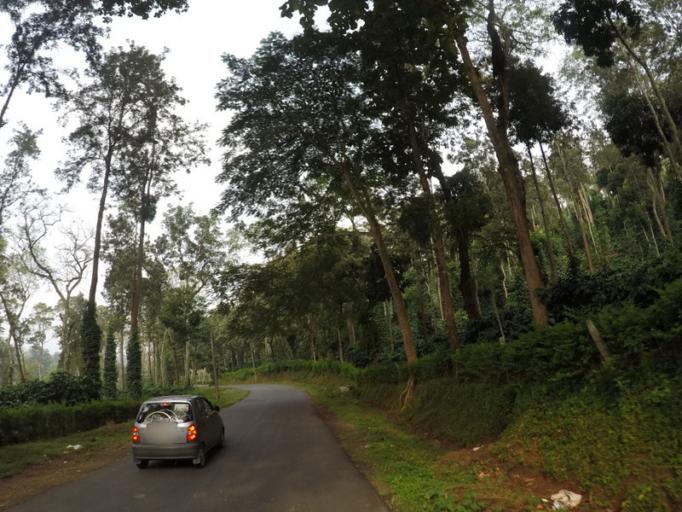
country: IN
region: Karnataka
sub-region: Chikmagalur
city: Koppa
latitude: 13.3487
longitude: 75.4807
